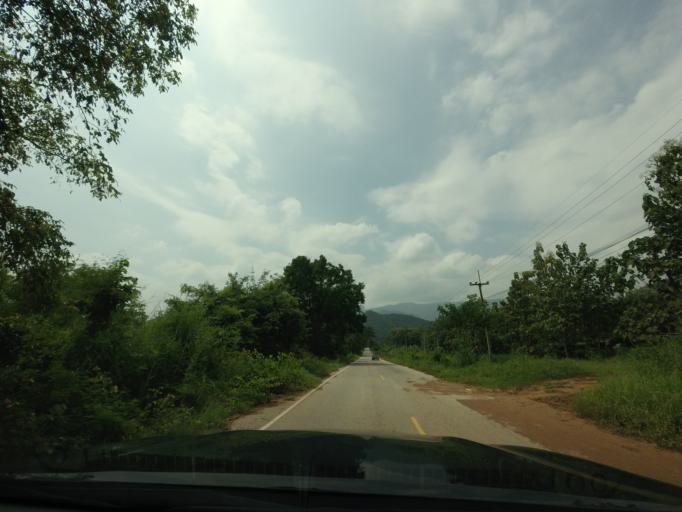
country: TH
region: Loei
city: Tha Li
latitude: 17.5873
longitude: 101.4147
